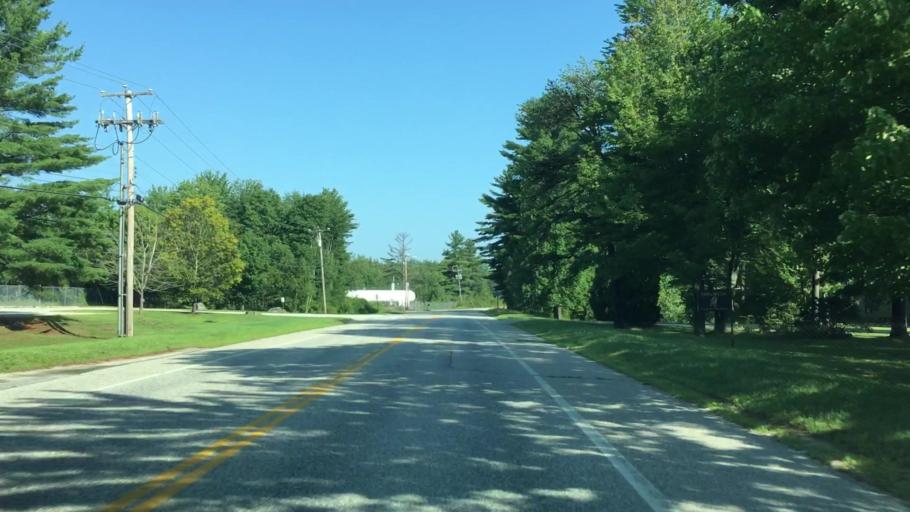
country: US
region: Maine
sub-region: Androscoggin County
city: Minot
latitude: 44.0447
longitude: -70.2941
